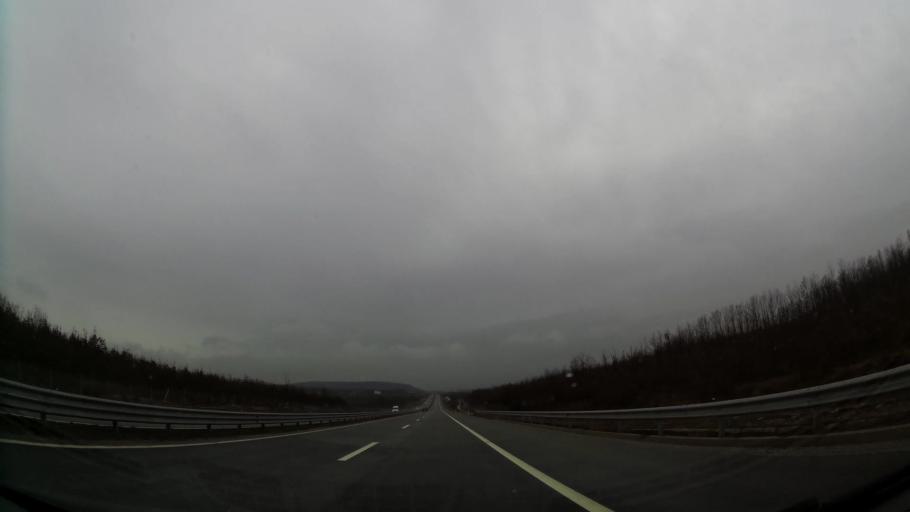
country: XK
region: Ferizaj
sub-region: Komuna e Ferizajt
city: Ferizaj
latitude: 42.3434
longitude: 21.2053
